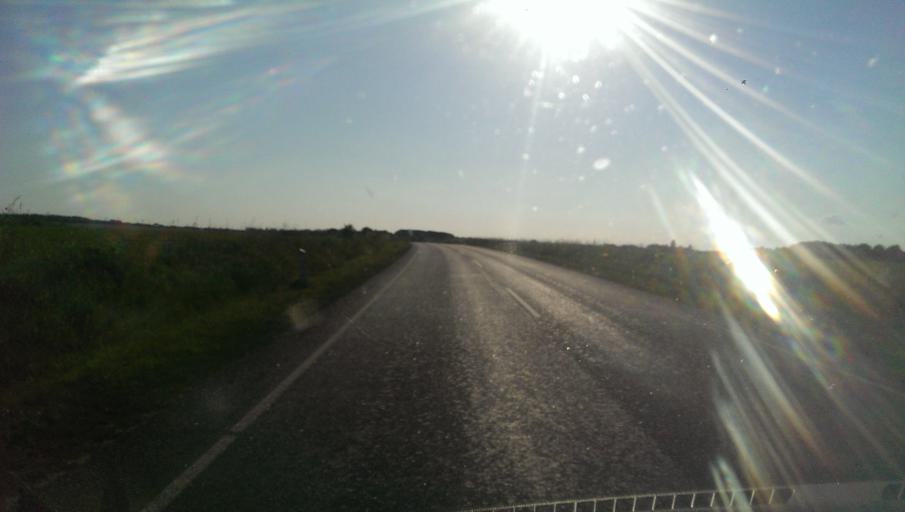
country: DK
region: South Denmark
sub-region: Esbjerg Kommune
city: Tjaereborg
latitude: 55.5266
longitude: 8.6290
